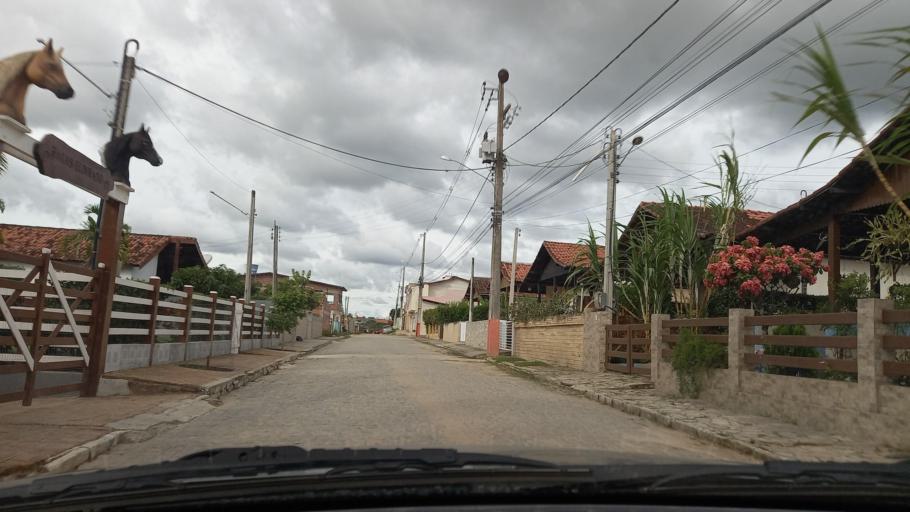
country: BR
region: Pernambuco
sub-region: Gravata
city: Gravata
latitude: -8.1977
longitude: -35.5490
